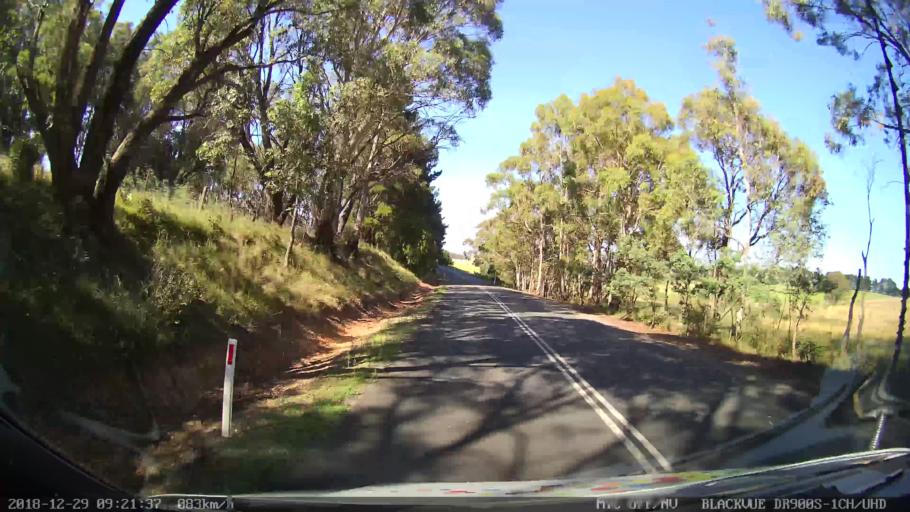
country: AU
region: New South Wales
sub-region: Upper Lachlan Shire
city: Crookwell
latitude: -34.5036
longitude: 149.4127
